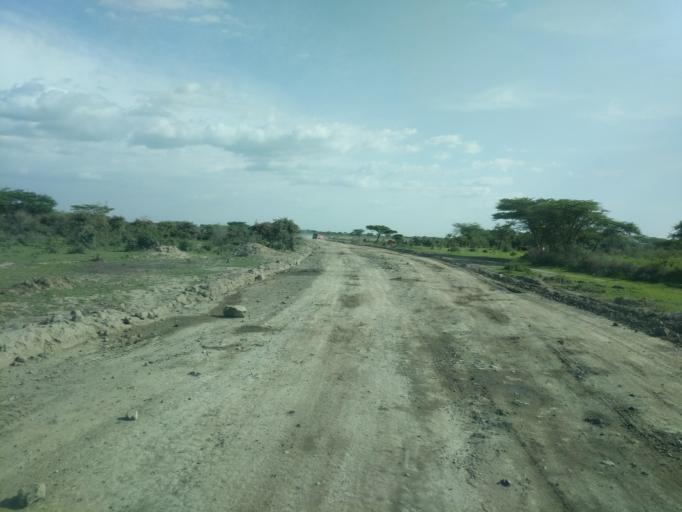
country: ET
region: Oromiya
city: Ziway
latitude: 7.5844
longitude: 38.6828
